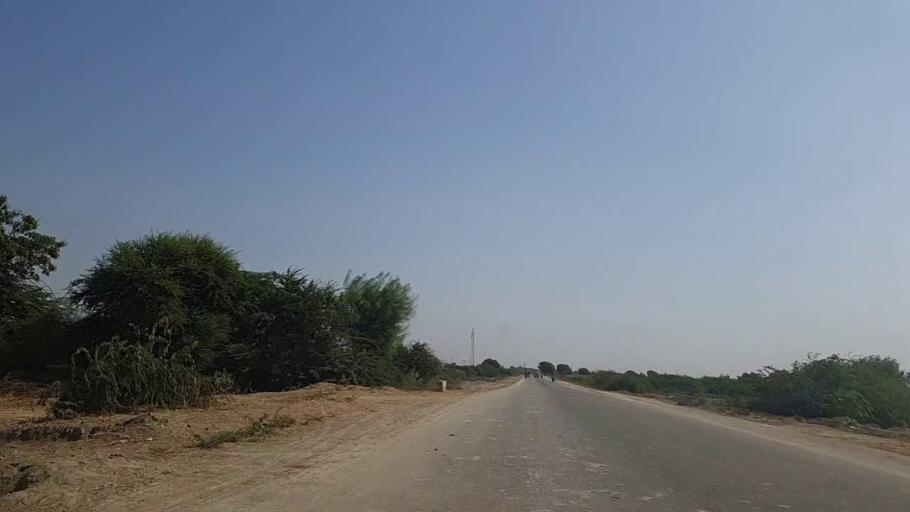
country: PK
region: Sindh
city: Mirpur Batoro
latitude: 24.7429
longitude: 68.2465
